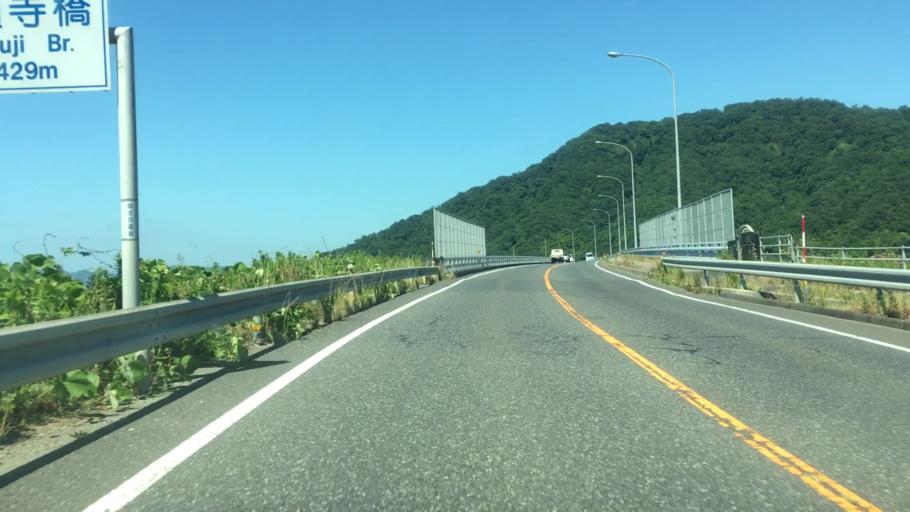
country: JP
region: Tottori
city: Tottori
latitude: 35.4379
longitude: 134.2064
